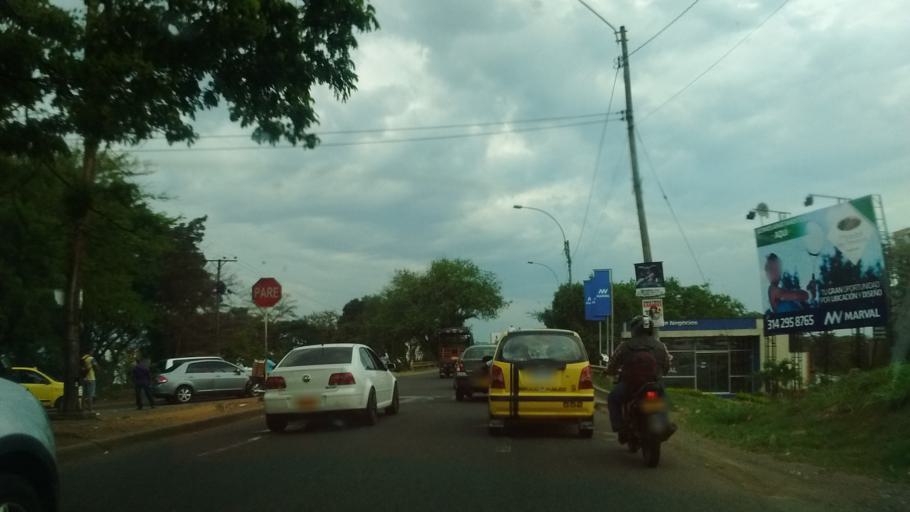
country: CO
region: Valle del Cauca
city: Cali
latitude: 3.3660
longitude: -76.5270
